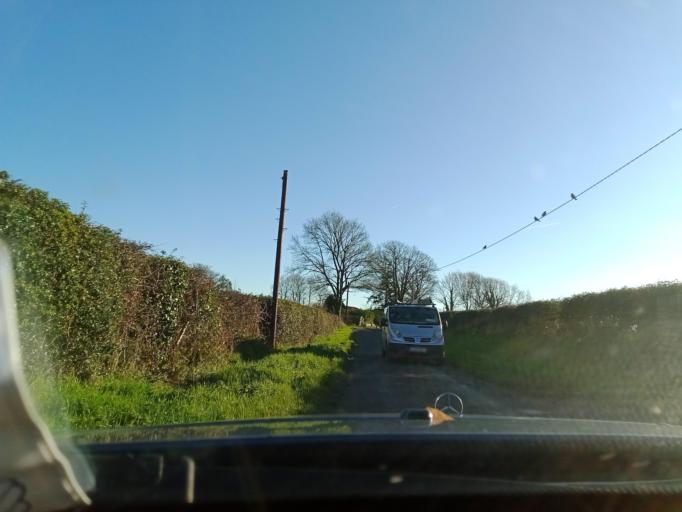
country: IE
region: Leinster
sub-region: Kilkenny
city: Mooncoin
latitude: 52.3055
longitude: -7.2259
